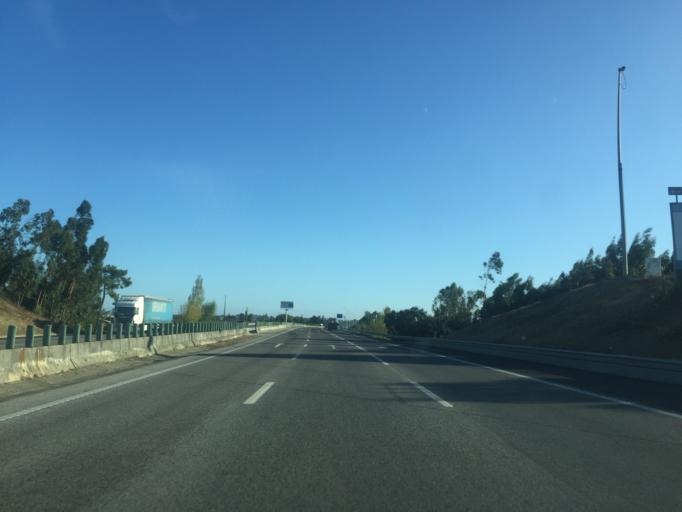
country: PT
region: Lisbon
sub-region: Azambuja
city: Aveiras de Cima
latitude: 39.1185
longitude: -8.9141
